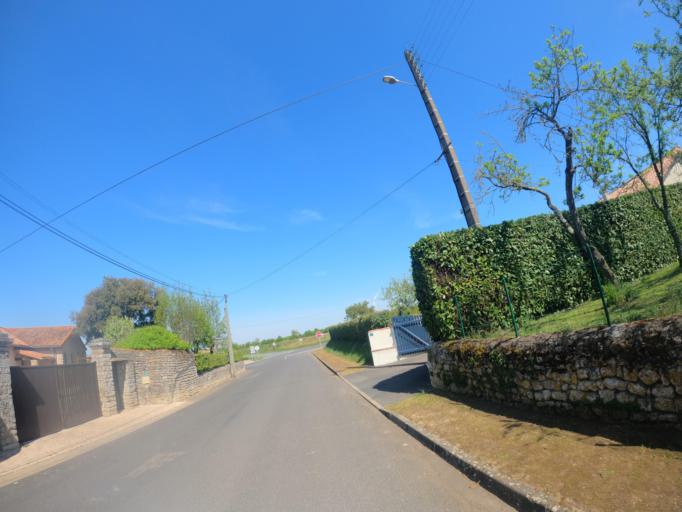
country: FR
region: Poitou-Charentes
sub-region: Departement des Deux-Sevres
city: Airvault
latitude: 46.8840
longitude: -0.1340
